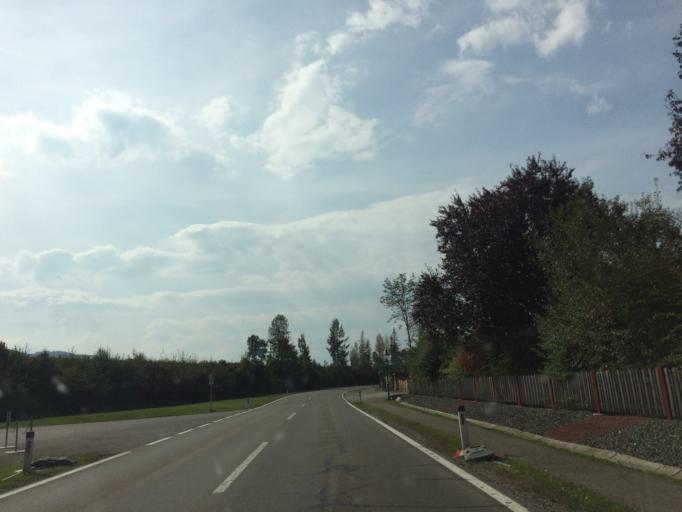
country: AT
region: Styria
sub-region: Politischer Bezirk Murtal
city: Feistritz bei Knittelfeld
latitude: 47.2586
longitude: 14.8992
